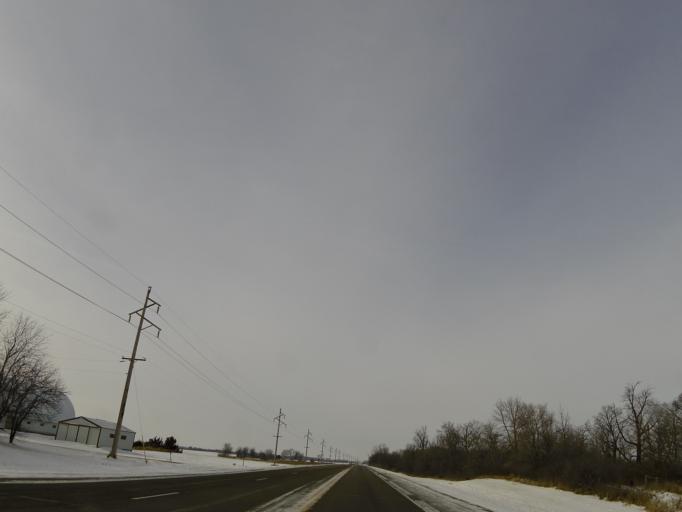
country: US
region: Minnesota
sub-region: Carver County
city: Mayer
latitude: 44.9056
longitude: -93.8508
